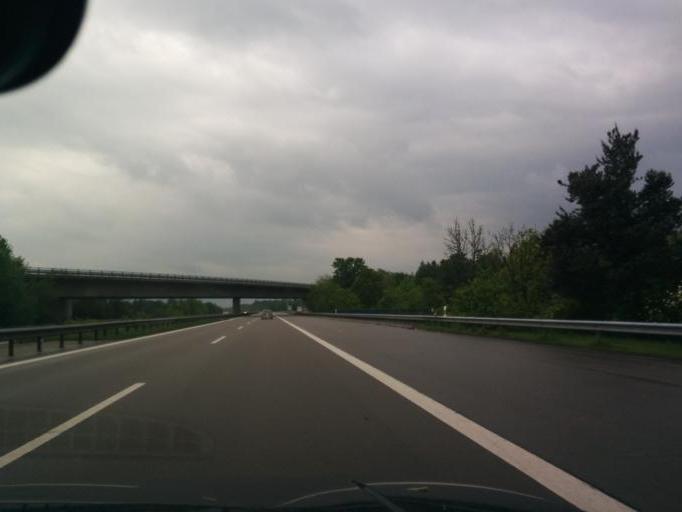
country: DE
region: Bavaria
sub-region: Upper Bavaria
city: Brunnthal
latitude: 48.0251
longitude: 11.6584
